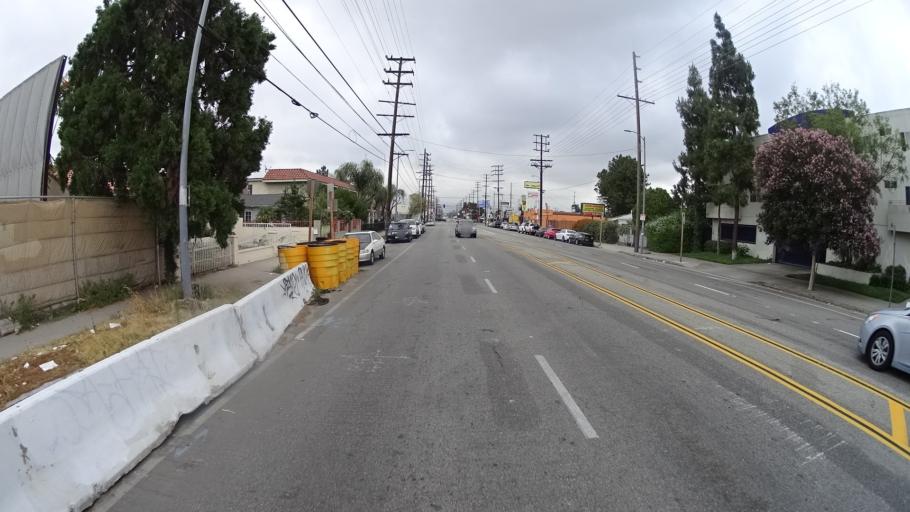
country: US
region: California
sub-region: Los Angeles County
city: North Hollywood
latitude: 34.1940
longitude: -118.3898
